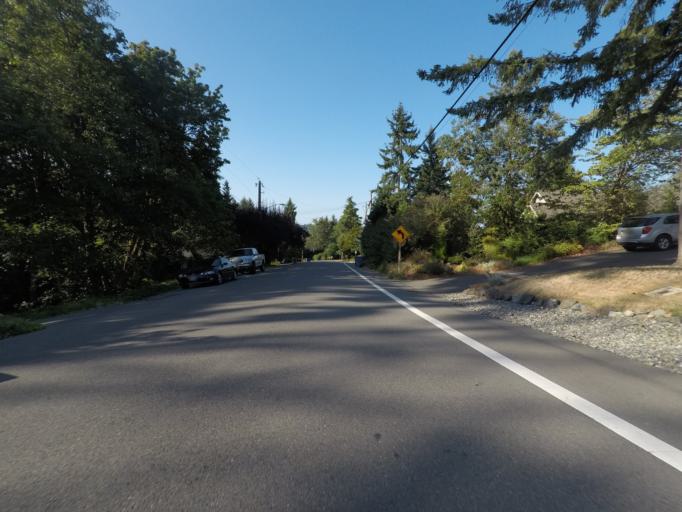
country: US
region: Washington
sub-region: King County
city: Kenmore
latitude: 47.7425
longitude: -122.2327
